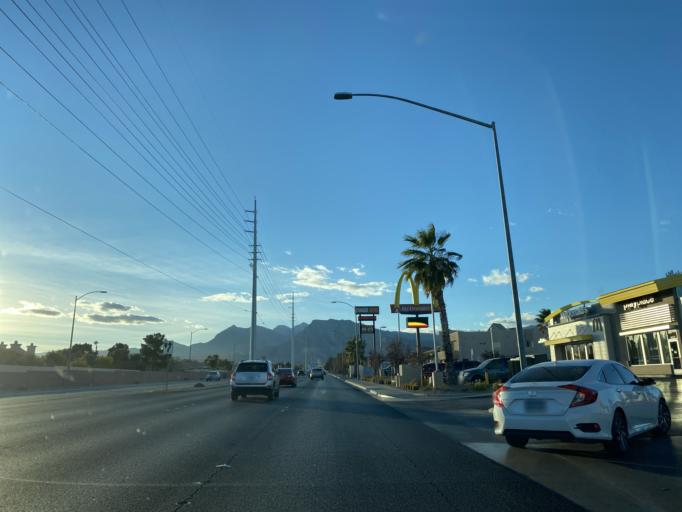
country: US
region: Nevada
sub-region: Clark County
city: Summerlin South
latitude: 36.2187
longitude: -115.2809
